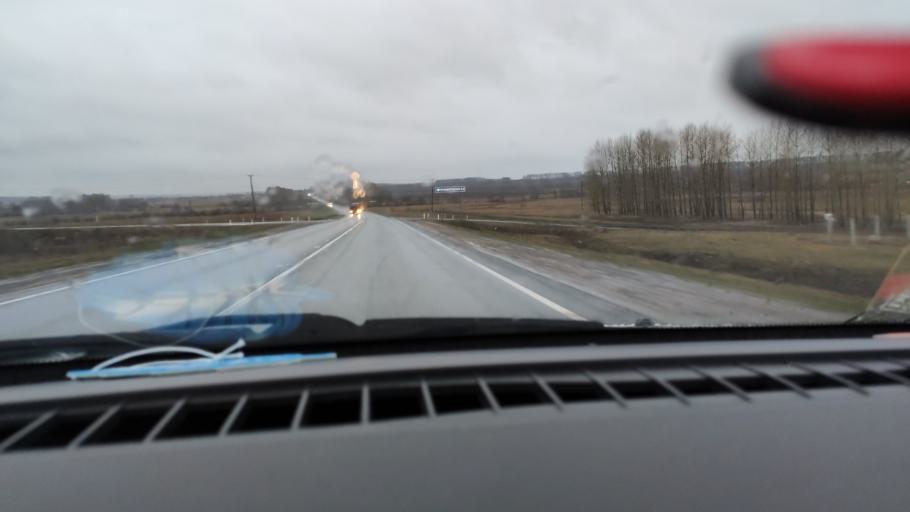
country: RU
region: Tatarstan
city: Mendeleyevsk
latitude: 55.9706
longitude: 52.3179
